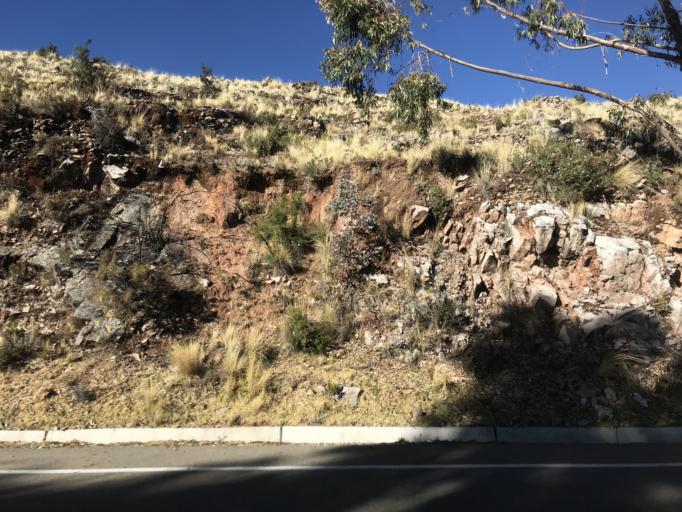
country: BO
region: La Paz
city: San Pedro
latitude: -16.1920
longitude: -68.9191
